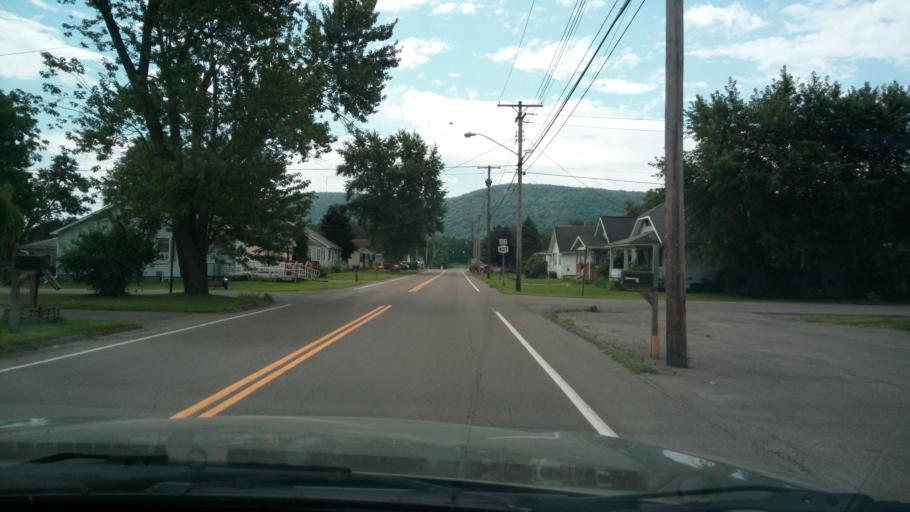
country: US
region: New York
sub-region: Chemung County
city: Southport
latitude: 42.0602
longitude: -76.7935
